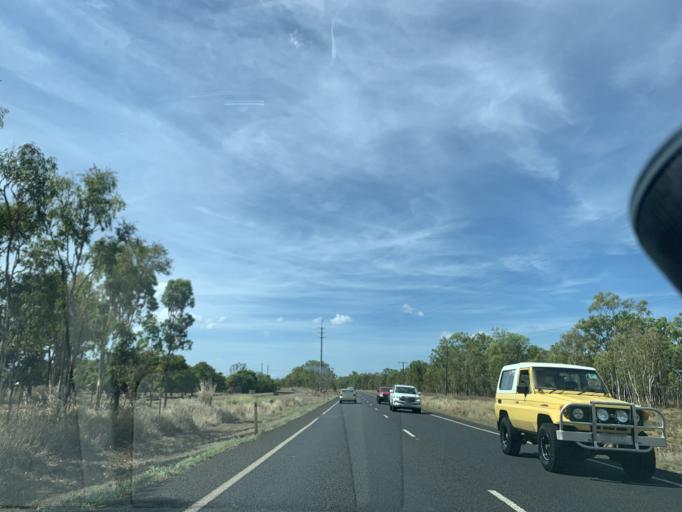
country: AU
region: Queensland
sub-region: Tablelands
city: Tolga
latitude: -17.1556
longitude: 145.4396
